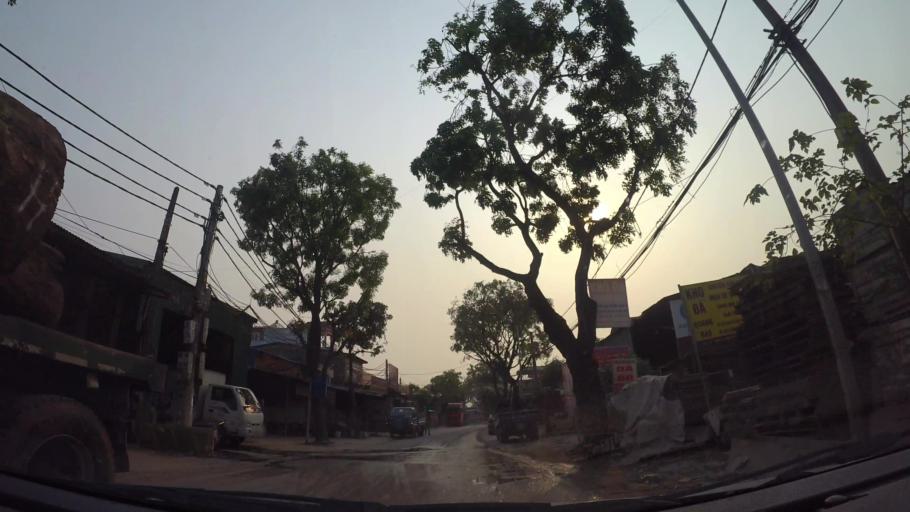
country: VN
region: Ha Noi
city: Ha Dong
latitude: 20.9952
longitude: 105.7428
